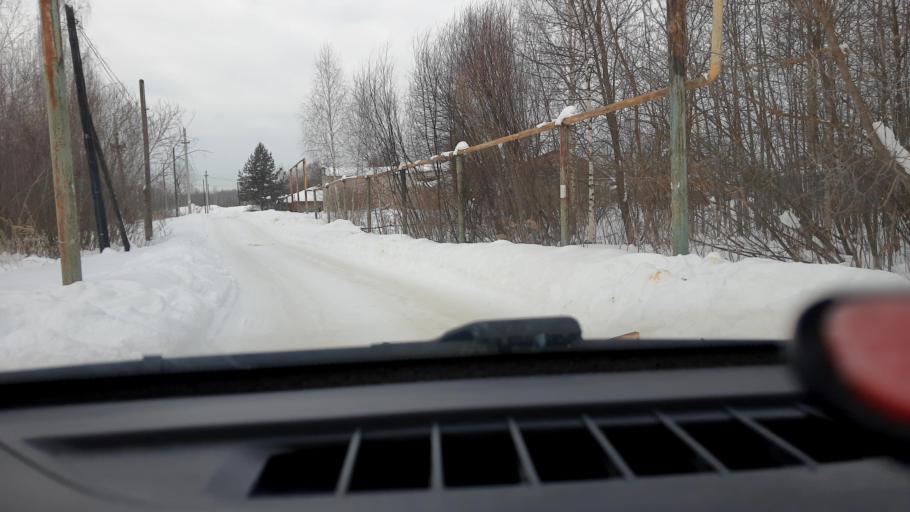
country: RU
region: Nizjnij Novgorod
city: Gorbatovka
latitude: 56.2547
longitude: 43.7361
